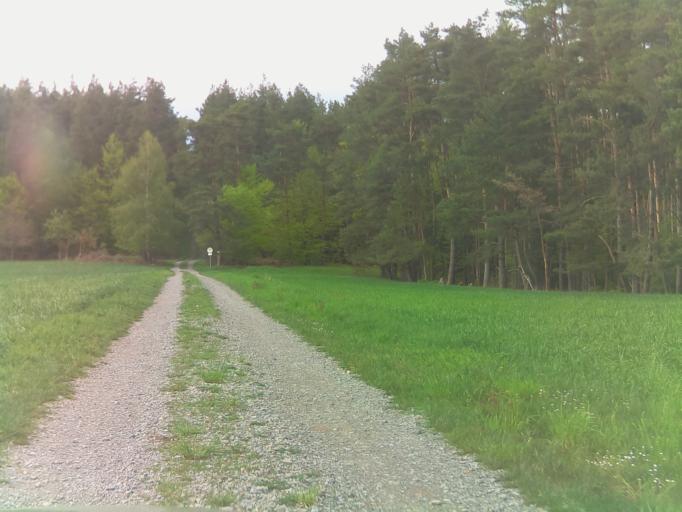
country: DE
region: Thuringia
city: Wahns
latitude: 50.6381
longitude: 10.3041
